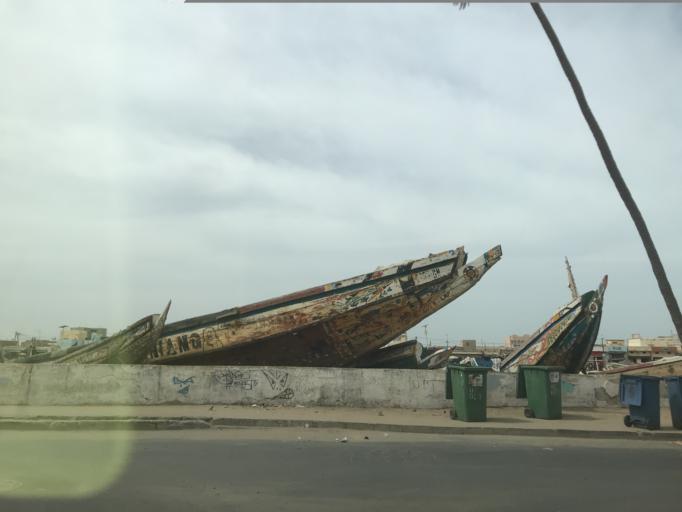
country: SN
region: Saint-Louis
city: Saint-Louis
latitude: 16.0270
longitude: -16.5062
